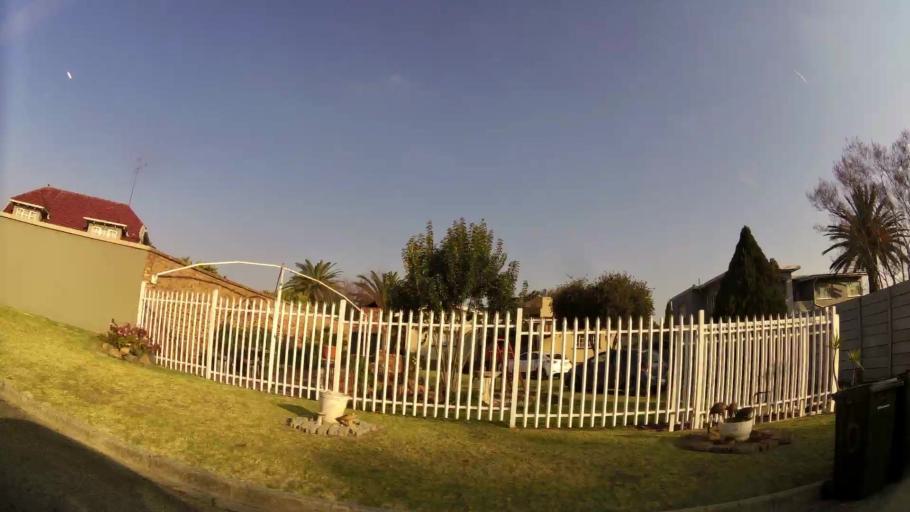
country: ZA
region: Gauteng
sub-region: Ekurhuleni Metropolitan Municipality
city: Springs
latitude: -26.2924
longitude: 28.4481
